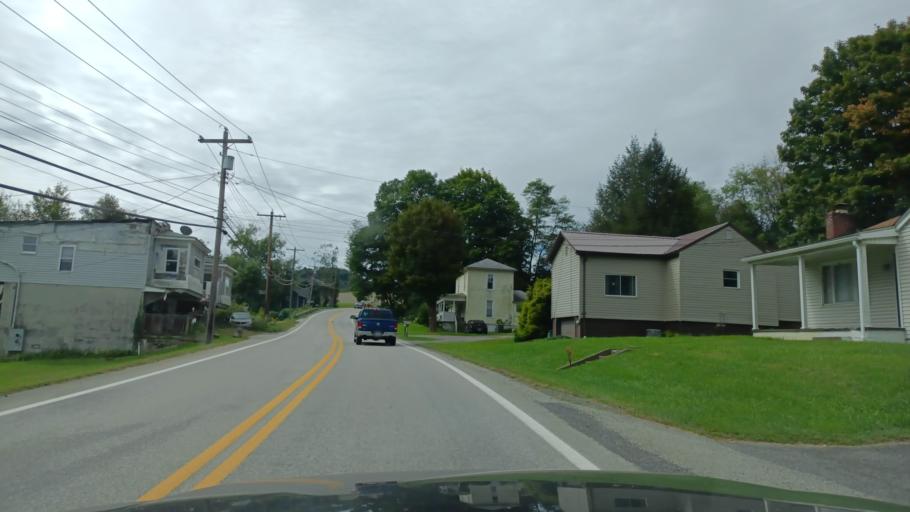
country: US
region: West Virginia
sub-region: Taylor County
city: Grafton
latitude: 39.3349
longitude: -80.0739
